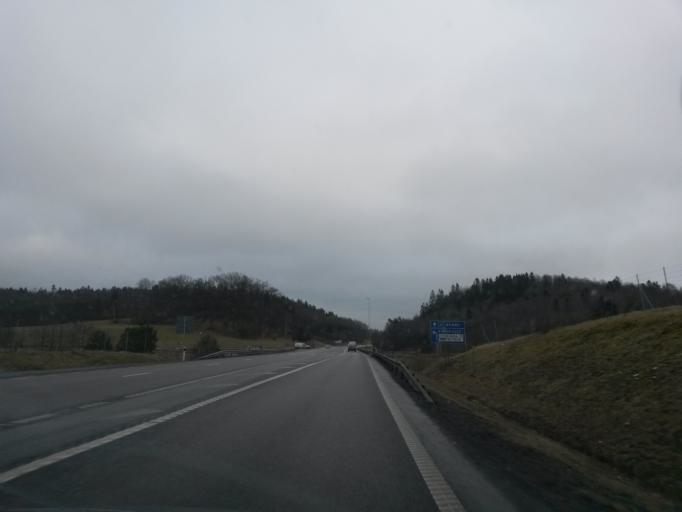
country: SE
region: Vaestra Goetaland
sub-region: Marks Kommun
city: Kinna
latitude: 57.5100
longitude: 12.7193
